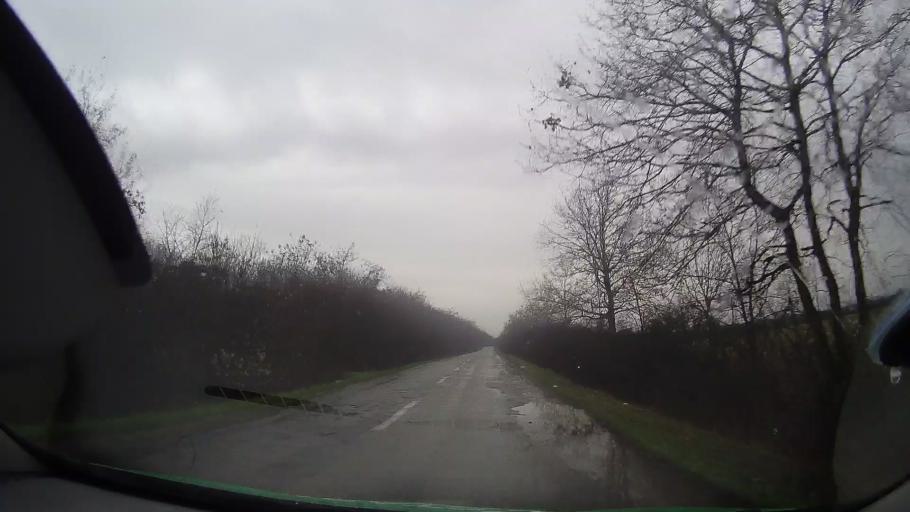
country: RO
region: Bihor
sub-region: Comuna Cociuba Mare
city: Cociuba Mare
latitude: 46.7424
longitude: 21.9730
